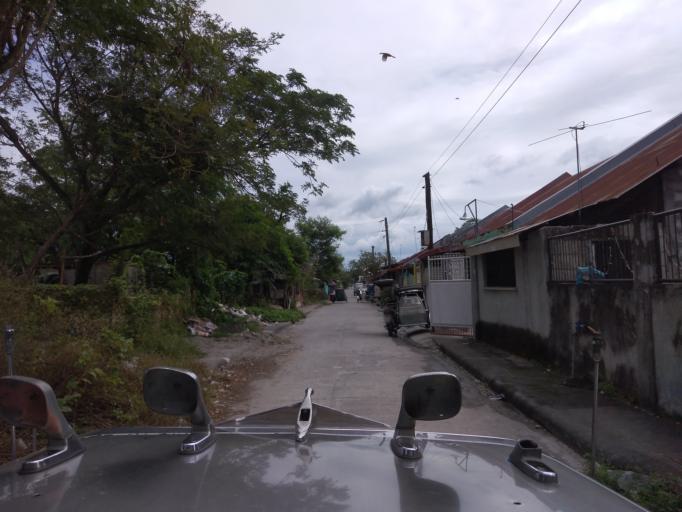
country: PH
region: Central Luzon
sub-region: Province of Pampanga
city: Pandacaqui
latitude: 15.1765
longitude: 120.6589
